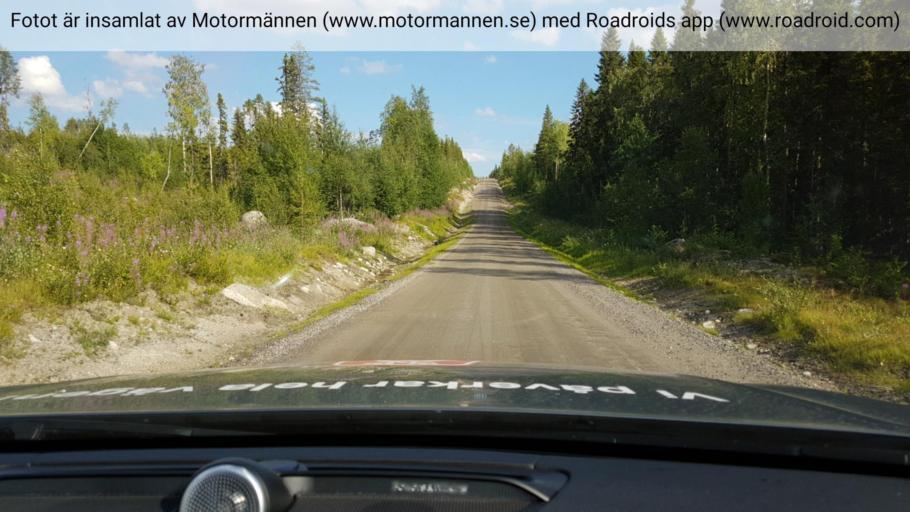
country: SE
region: Vaesterbotten
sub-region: Dorotea Kommun
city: Dorotea
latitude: 63.9314
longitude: 16.1117
